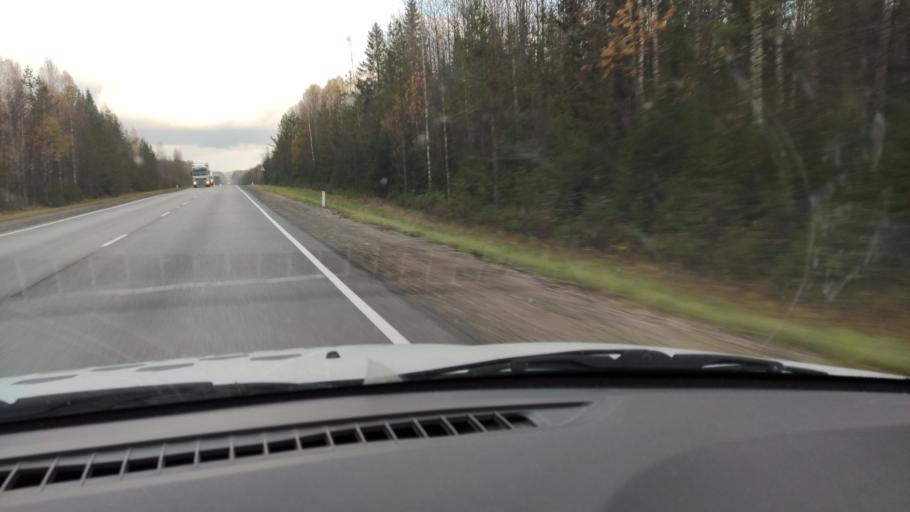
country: RU
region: Kirov
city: Chernaya Kholunitsa
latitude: 58.8135
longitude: 51.8281
